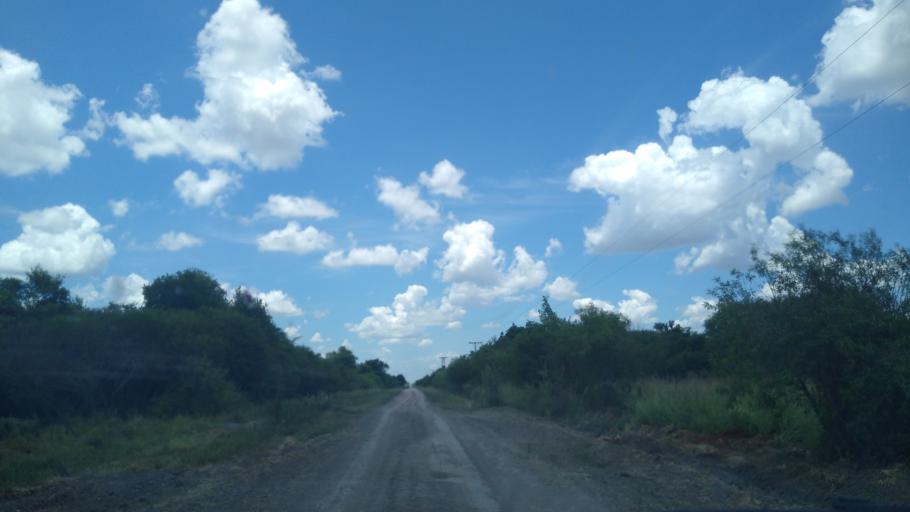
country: AR
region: Chaco
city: Presidencia Roque Saenz Pena
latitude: -26.7466
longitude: -60.3359
